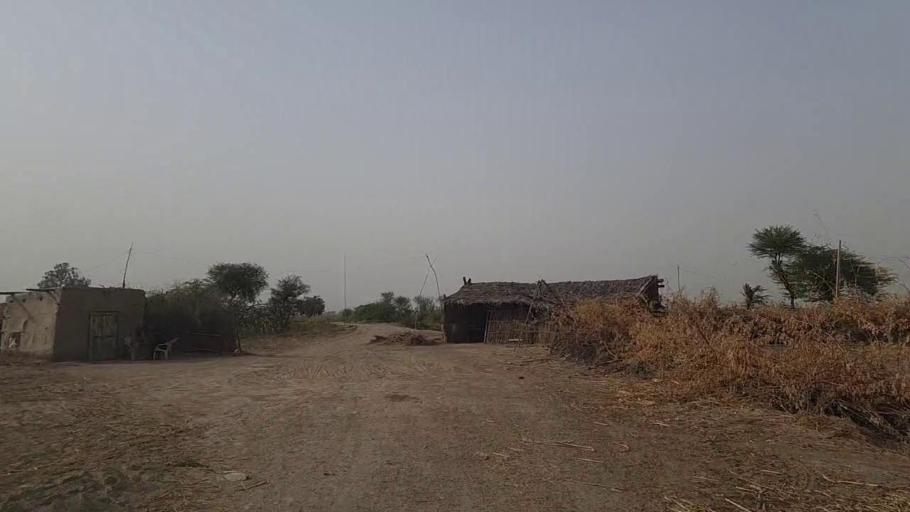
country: PK
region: Sindh
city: Pithoro
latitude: 25.4279
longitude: 69.2847
